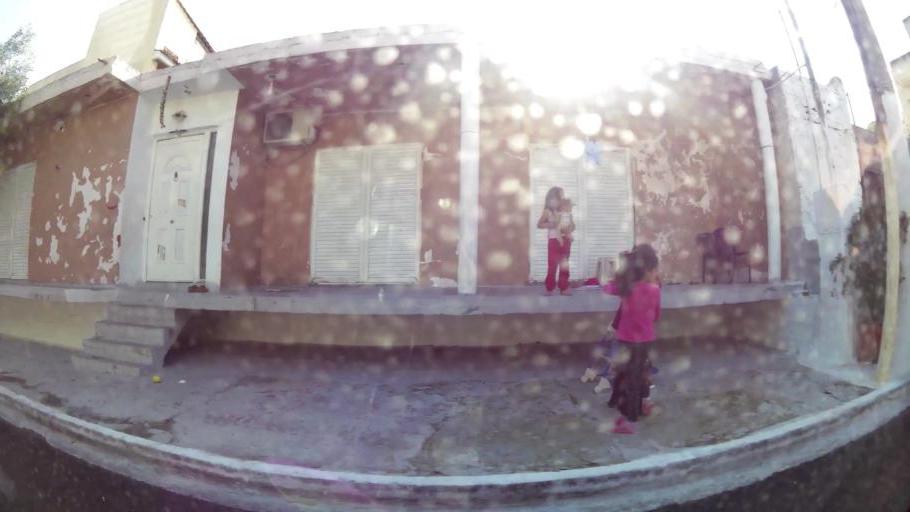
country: GR
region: Attica
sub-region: Nomarchia Dytikis Attikis
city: Zefyri
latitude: 38.0749
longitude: 23.7167
